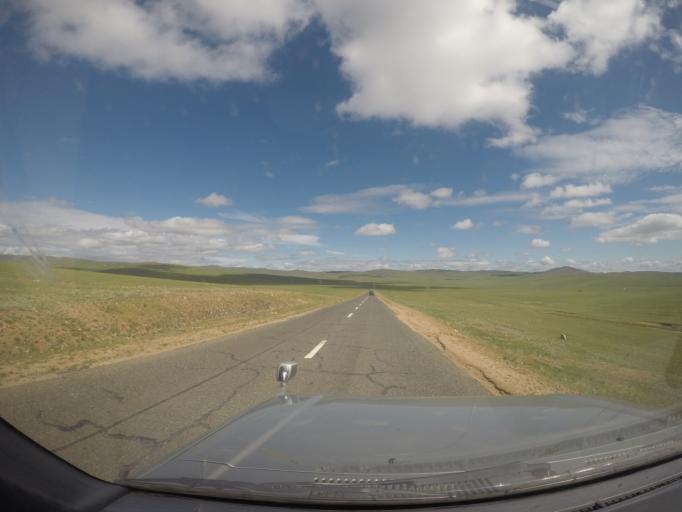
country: MN
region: Hentiy
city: Modot
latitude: 47.6075
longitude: 109.2076
